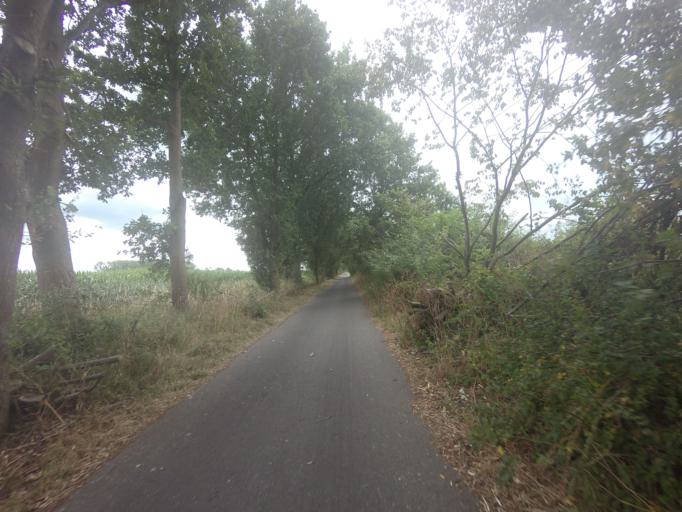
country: NL
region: North Holland
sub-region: Gemeente Wijdemeren
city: Nieuw-Loosdrecht
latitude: 52.1711
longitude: 5.1822
